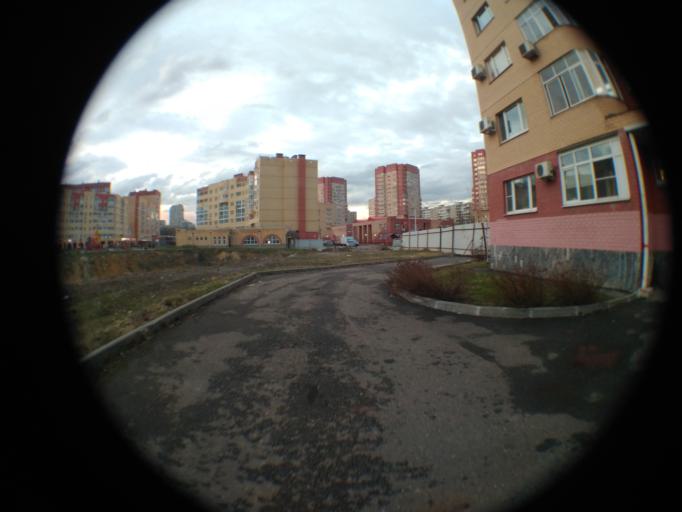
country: RU
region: Moskovskaya
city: Bykovo
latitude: 55.6025
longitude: 38.0865
